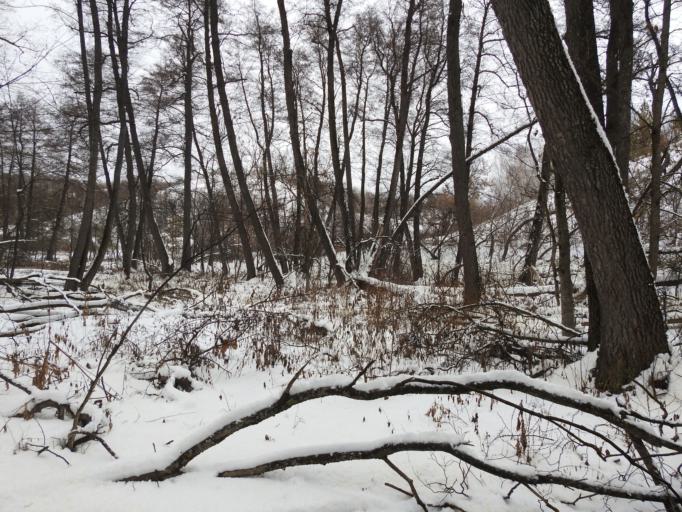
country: RU
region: Saratov
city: Tersa
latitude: 52.1075
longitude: 47.4723
